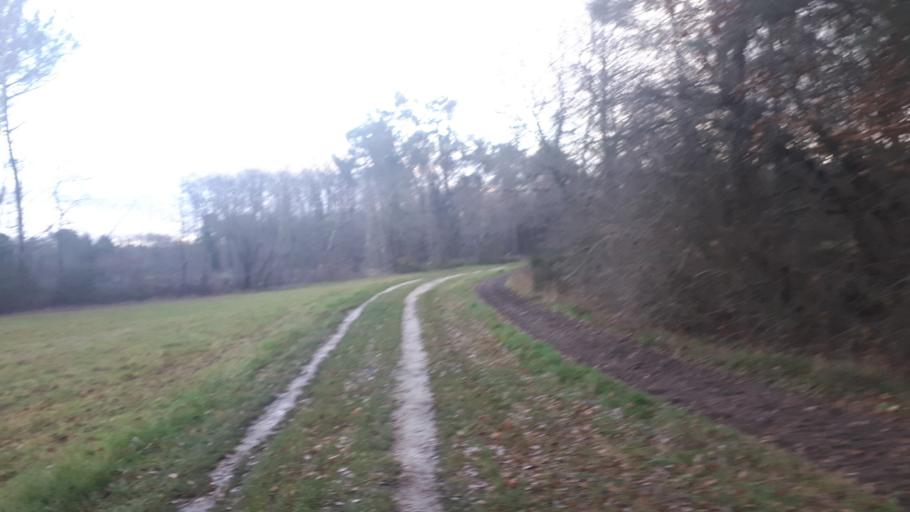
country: FR
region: Centre
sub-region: Departement du Loir-et-Cher
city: Saint-Romain-sur-Cher
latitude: 47.3455
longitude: 1.3952
